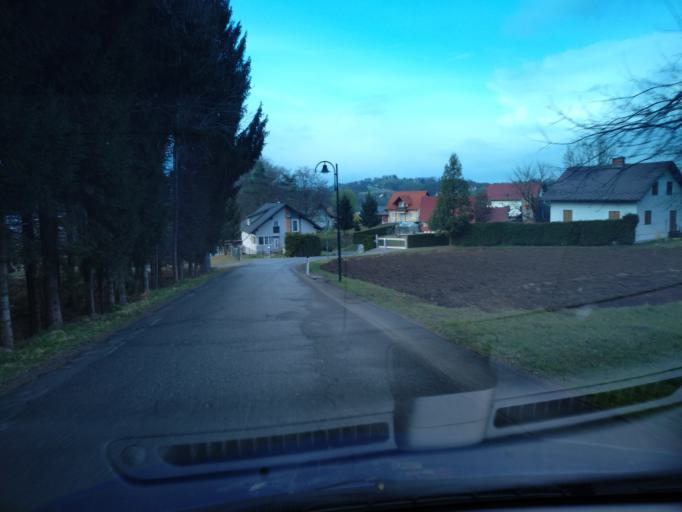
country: AT
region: Styria
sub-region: Politischer Bezirk Deutschlandsberg
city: Pitschgau
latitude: 46.6902
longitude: 15.2624
